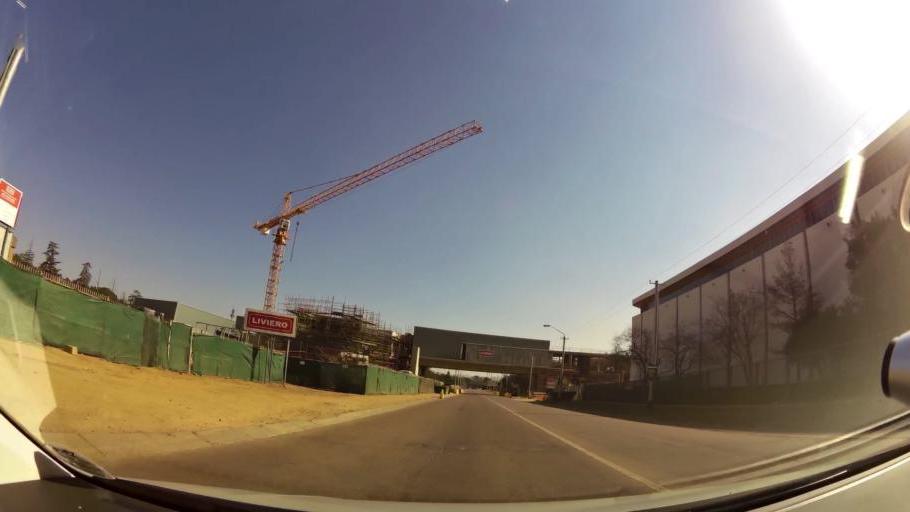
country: ZA
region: Gauteng
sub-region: City of Tshwane Metropolitan Municipality
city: Pretoria
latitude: -25.7565
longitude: 28.2294
